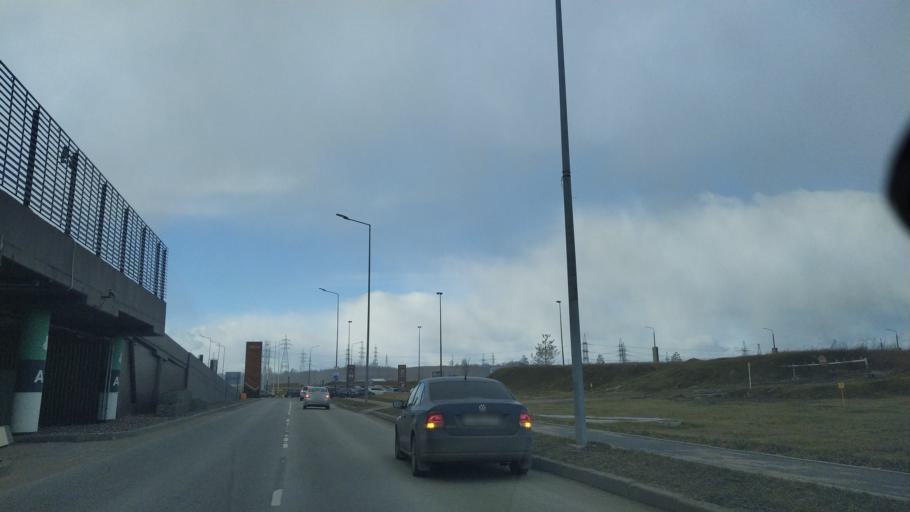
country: RU
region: Leningrad
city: Bugry
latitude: 60.0930
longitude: 30.3819
